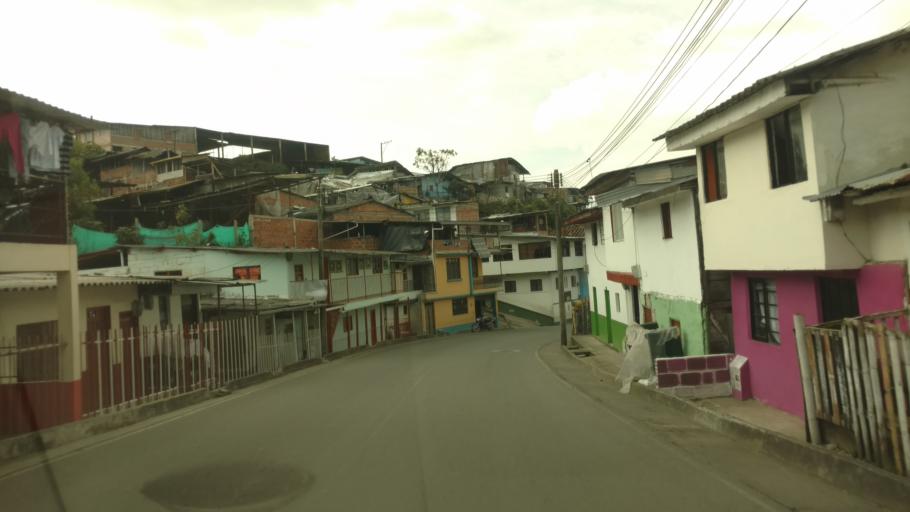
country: CO
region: Caldas
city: Neira
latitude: 5.1669
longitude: -75.5181
